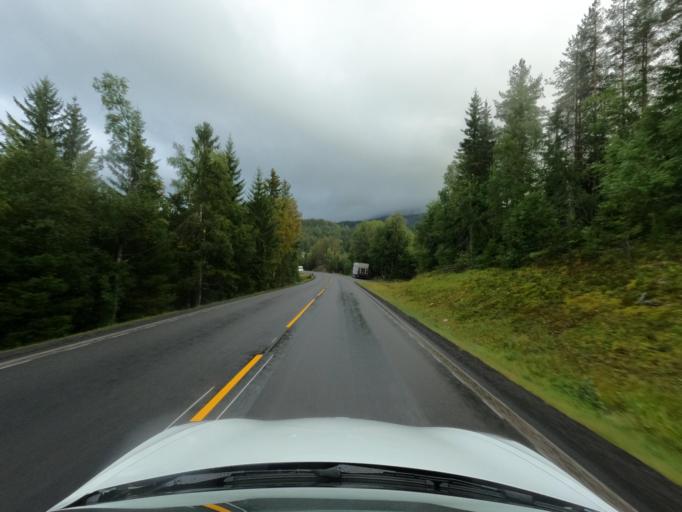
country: NO
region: Telemark
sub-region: Kviteseid
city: Kviteseid
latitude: 59.4428
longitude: 8.5171
